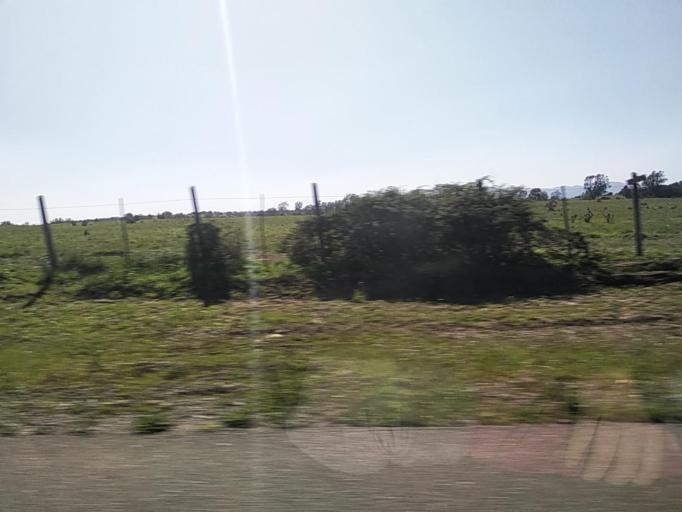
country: CL
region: Valparaiso
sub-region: San Antonio Province
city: El Tabo
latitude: -33.4068
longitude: -71.5429
